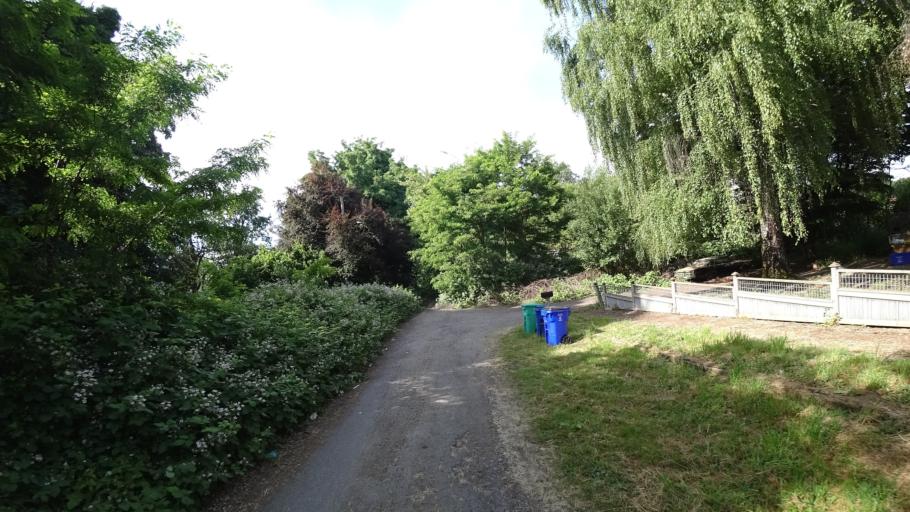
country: US
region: Washington
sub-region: Clark County
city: Vancouver
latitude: 45.5997
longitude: -122.7348
